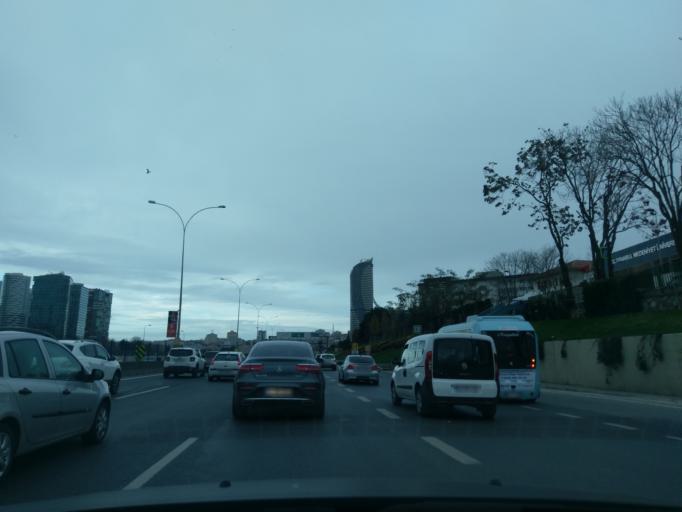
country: TR
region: Istanbul
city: UEskuedar
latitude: 40.9957
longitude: 29.0651
